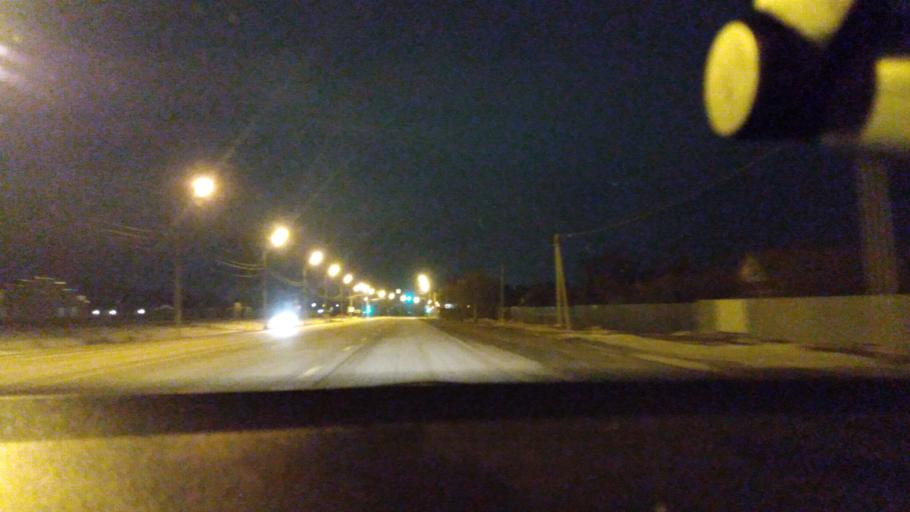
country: RU
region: Moskovskaya
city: Bronnitsy
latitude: 55.4009
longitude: 38.3086
